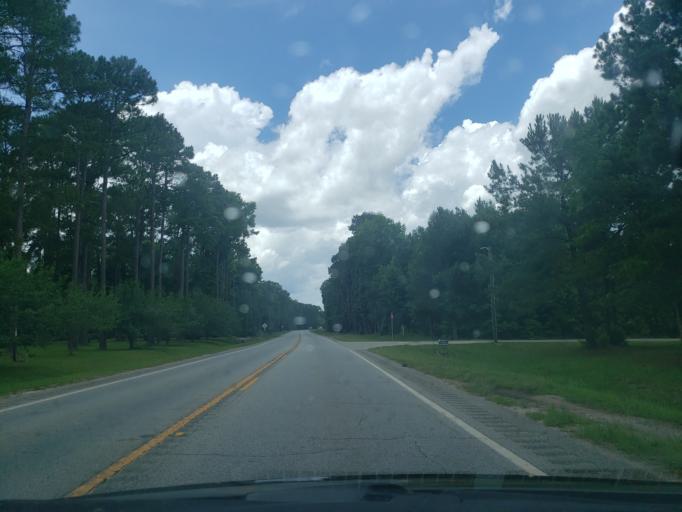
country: US
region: Georgia
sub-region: Bryan County
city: Richmond Hill
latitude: 32.0186
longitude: -81.3113
